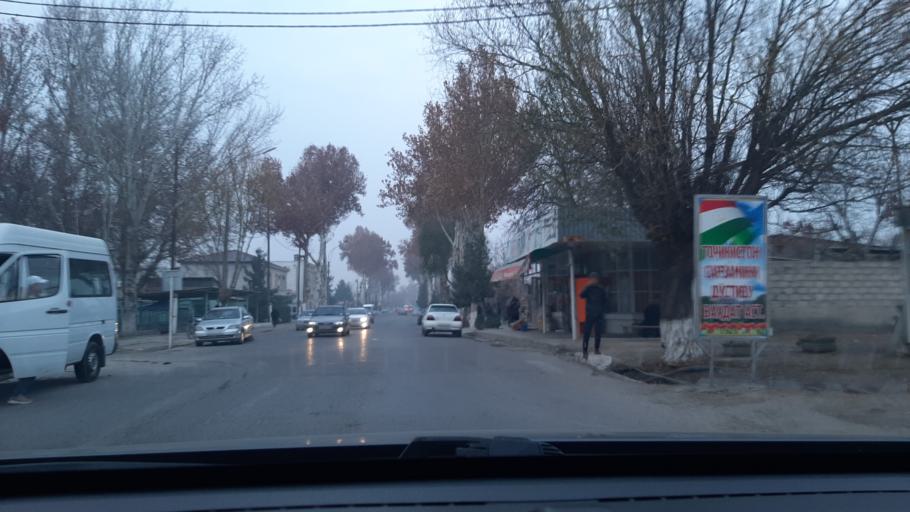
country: TJ
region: Viloyati Sughd
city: Khujand
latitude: 40.2638
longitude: 69.5994
